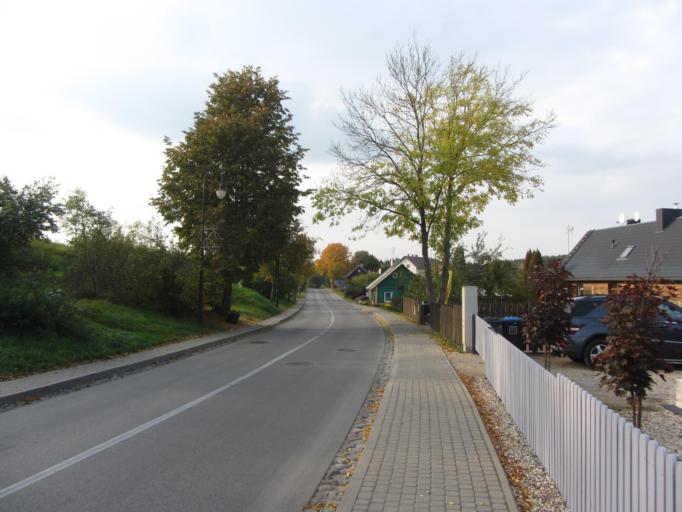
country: LT
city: Trakai
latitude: 54.6523
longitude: 24.9213
